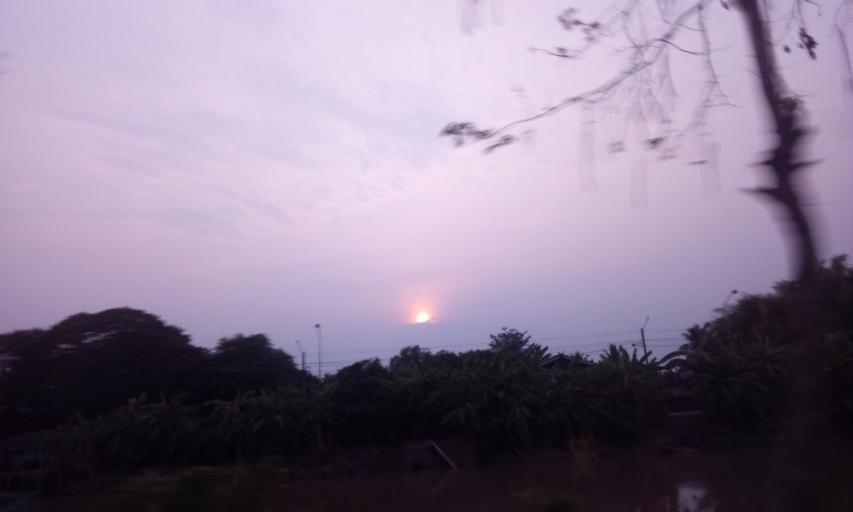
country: TH
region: Pathum Thani
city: Ban Lam Luk Ka
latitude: 13.9817
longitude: 100.8954
